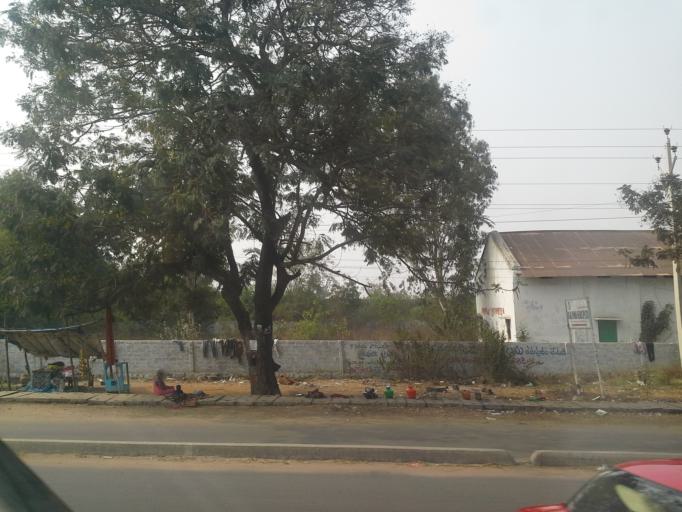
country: IN
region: Telangana
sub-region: Medak
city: Patancheru
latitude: 17.5253
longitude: 78.2710
